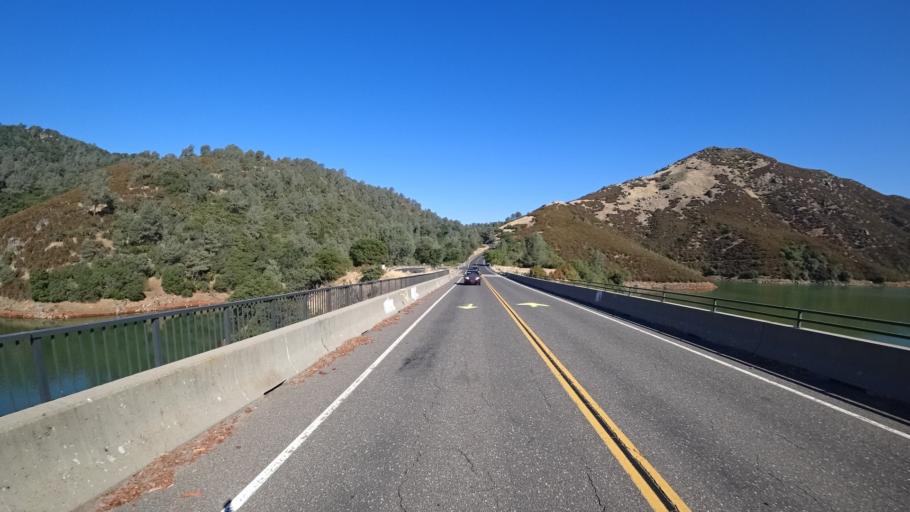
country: US
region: California
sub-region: Tuolumne County
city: Columbia
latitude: 38.0394
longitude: -120.4554
